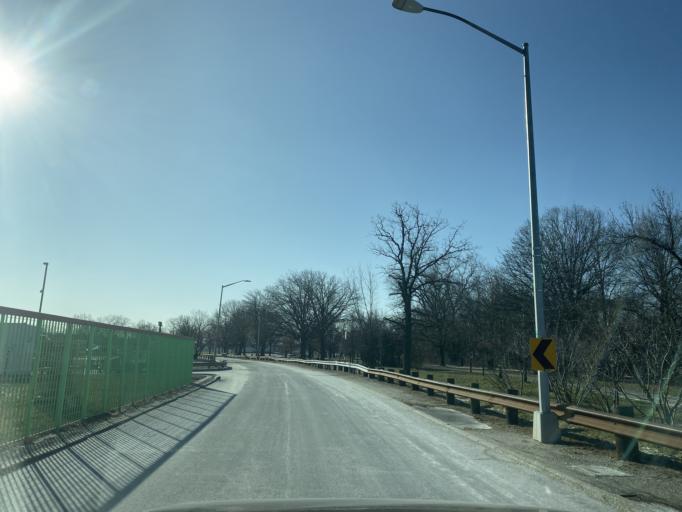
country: US
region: New York
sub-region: Bronx
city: The Bronx
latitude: 40.8145
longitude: -73.8380
